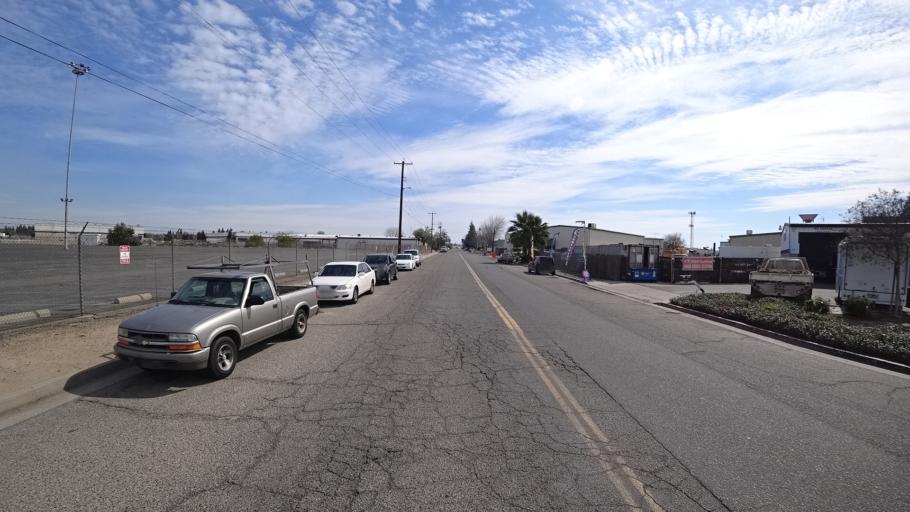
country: US
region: California
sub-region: Fresno County
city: West Park
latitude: 36.8154
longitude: -119.8951
